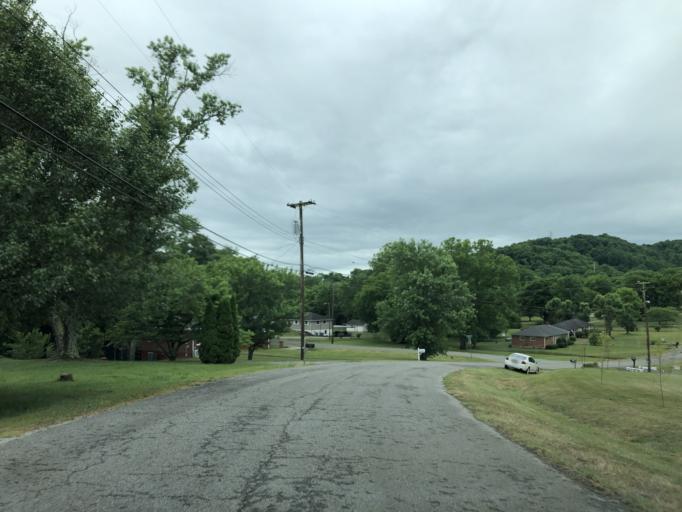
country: US
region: Tennessee
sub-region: Davidson County
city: Goodlettsville
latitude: 36.2675
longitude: -86.7723
